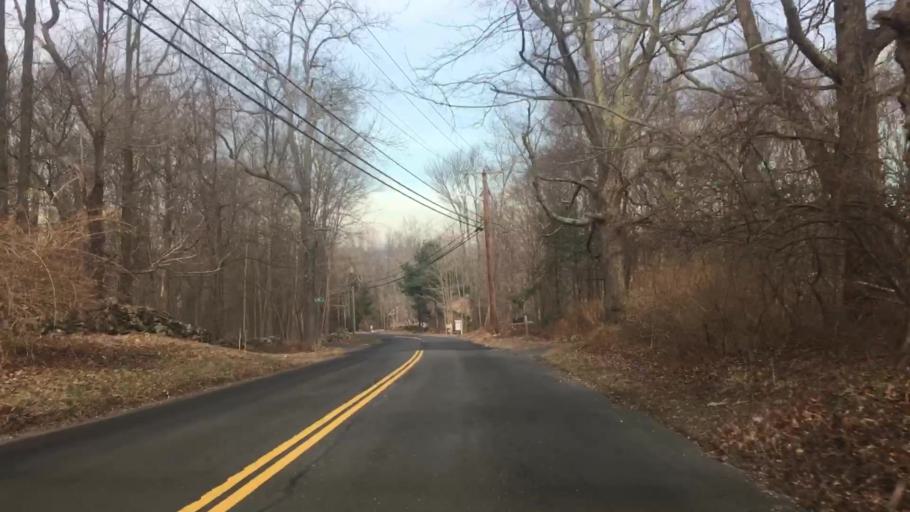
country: US
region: Connecticut
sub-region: Fairfield County
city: Newtown
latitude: 41.3972
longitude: -73.2586
